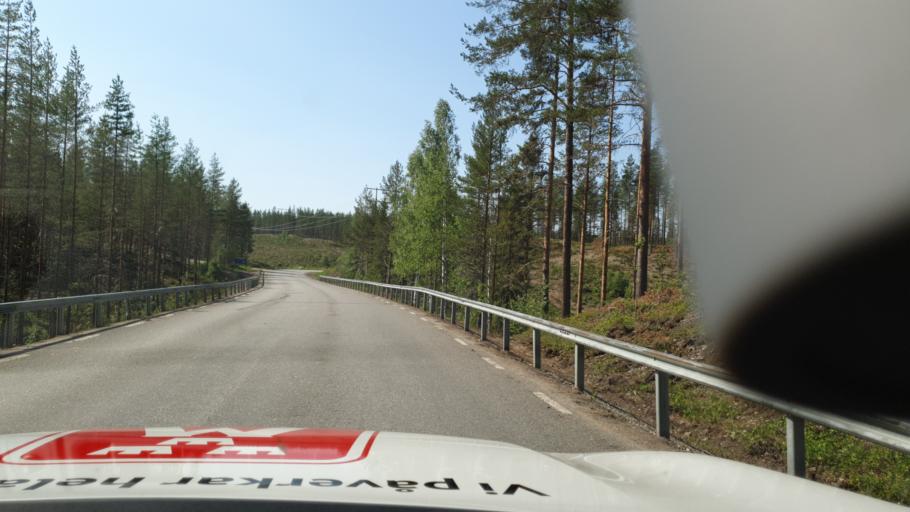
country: SE
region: Vaesterbotten
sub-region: Skelleftea Kommun
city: Langsele
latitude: 64.9431
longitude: 20.0338
